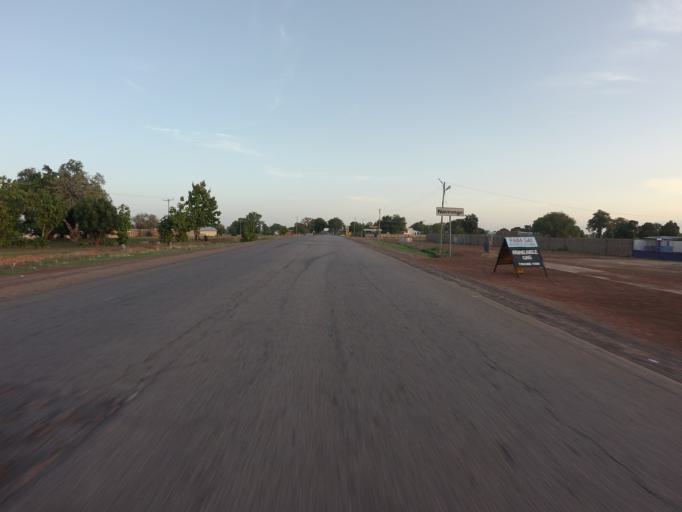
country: GH
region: Upper East
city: Navrongo
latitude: 10.9253
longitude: -1.0891
